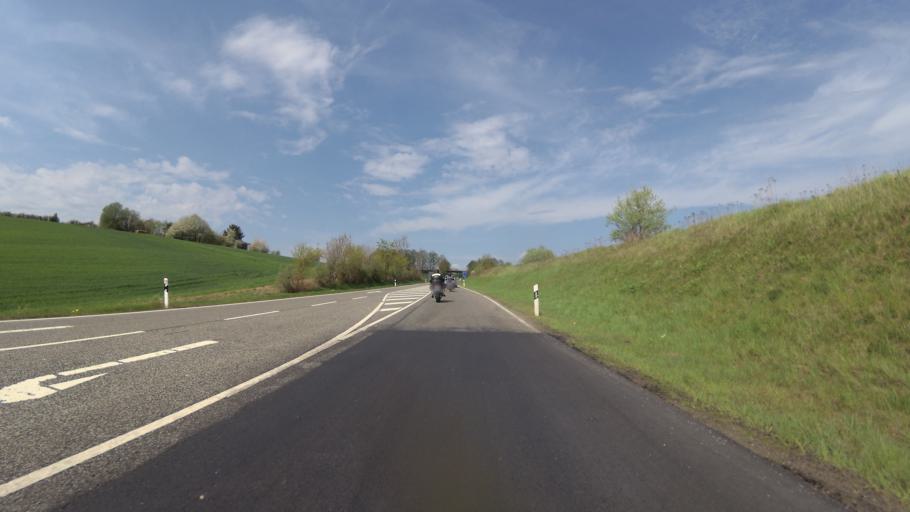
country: DE
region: Rheinland-Pfalz
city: Ulmen
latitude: 50.2026
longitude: 6.9789
